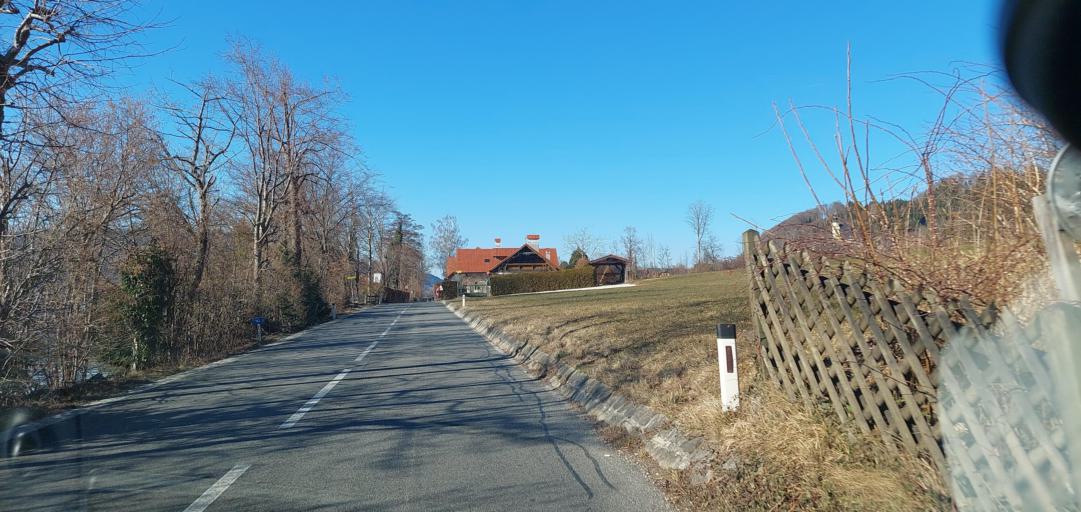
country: AT
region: Upper Austria
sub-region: Politischer Bezirk Vocklabruck
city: Steinbach am Attersee
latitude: 47.8254
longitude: 13.5474
